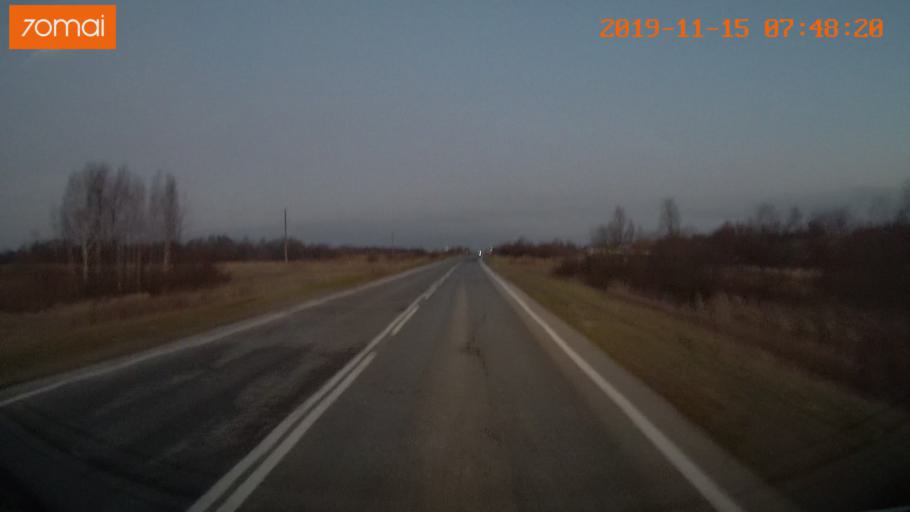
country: RU
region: Vologda
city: Cherepovets
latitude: 58.8501
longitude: 38.2450
